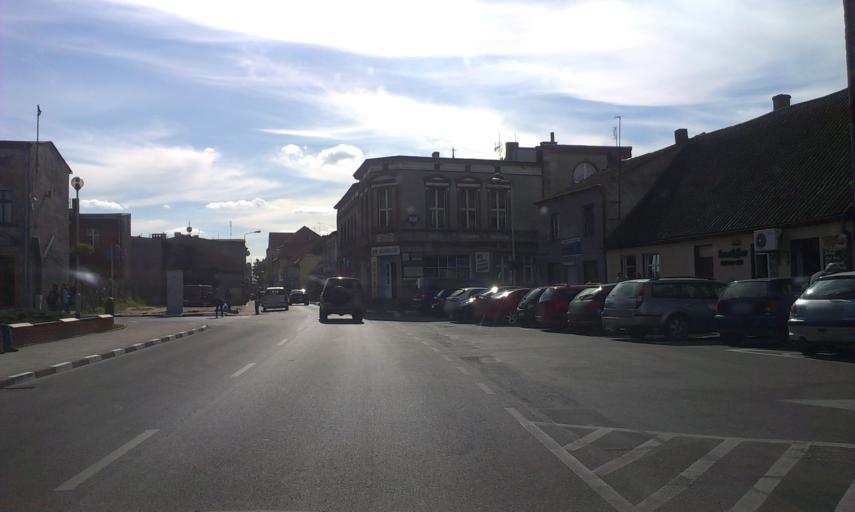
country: PL
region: Greater Poland Voivodeship
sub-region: Powiat pilski
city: Lobzenica
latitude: 53.2605
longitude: 17.2554
